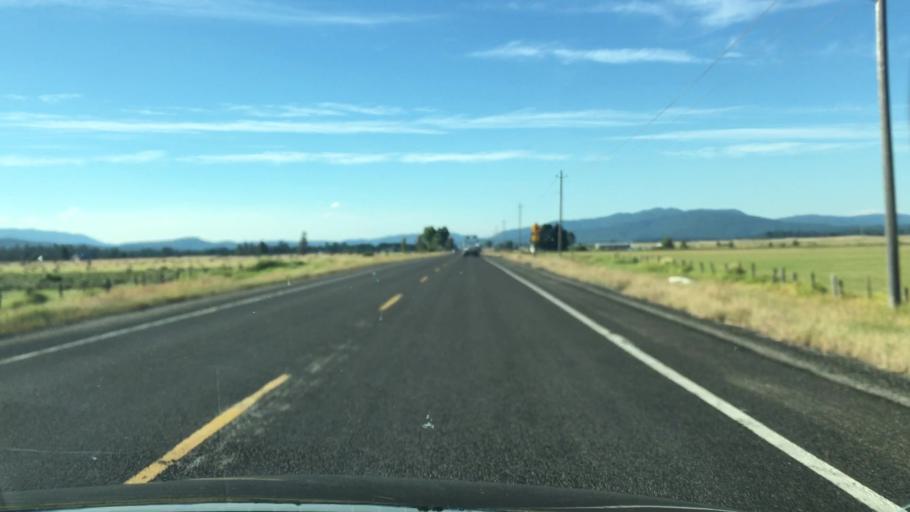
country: US
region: Idaho
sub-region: Valley County
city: Cascade
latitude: 44.4210
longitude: -115.9996
